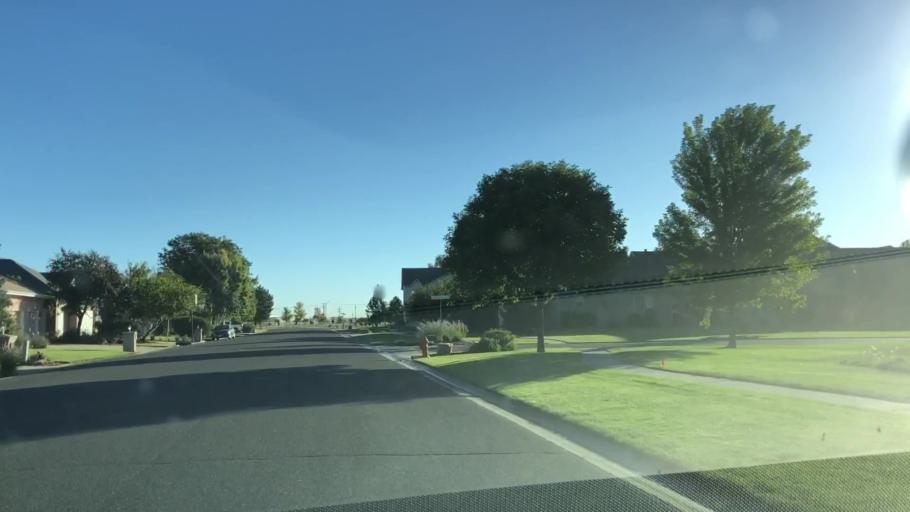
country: US
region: Colorado
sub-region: Larimer County
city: Loveland
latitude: 40.4335
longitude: -105.0246
